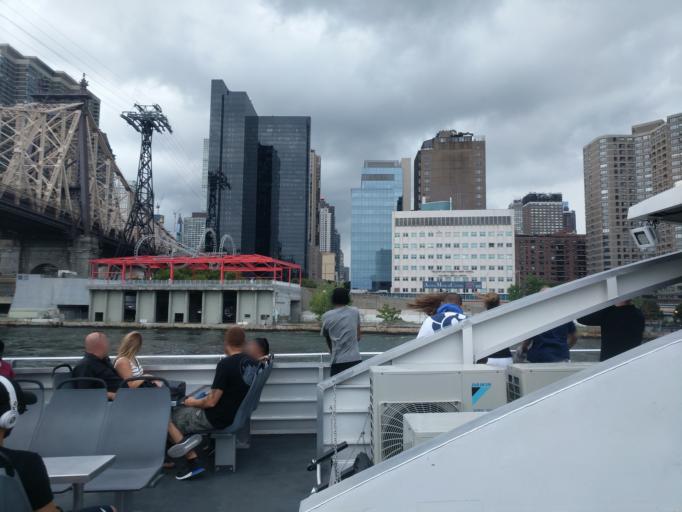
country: US
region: New York
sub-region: Queens County
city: Long Island City
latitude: 40.7590
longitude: -73.9563
